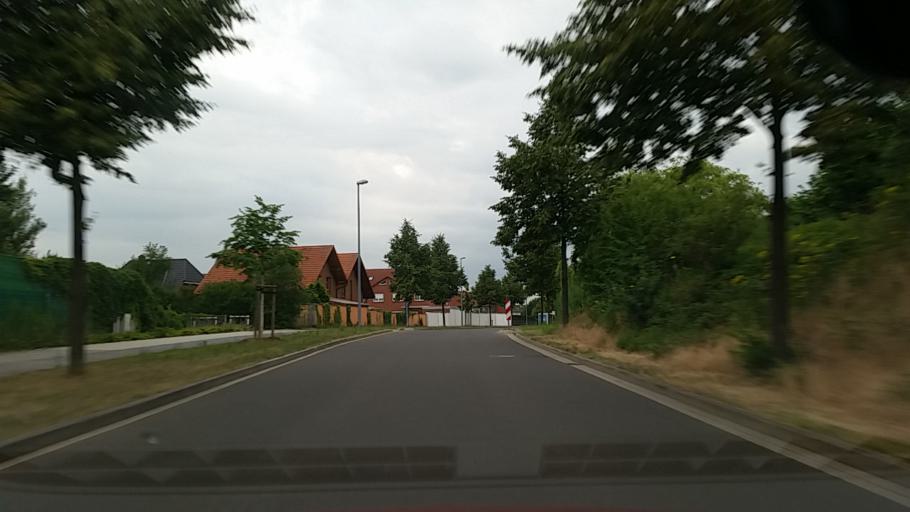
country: DE
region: Lower Saxony
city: Wolfsburg
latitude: 52.4187
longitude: 10.7470
